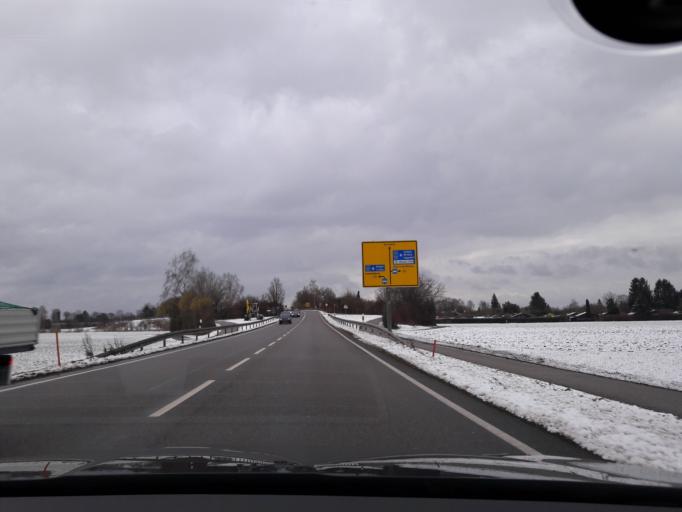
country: DE
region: Bavaria
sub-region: Upper Bavaria
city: Karlsfeld
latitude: 48.2508
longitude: 11.4736
